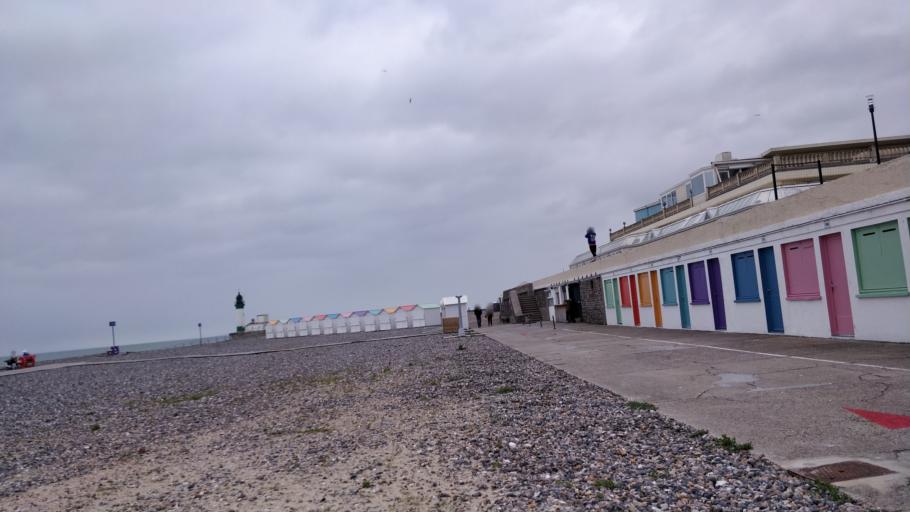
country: FR
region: Haute-Normandie
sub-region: Departement de la Seine-Maritime
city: Le Treport
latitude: 50.0625
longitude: 1.3676
